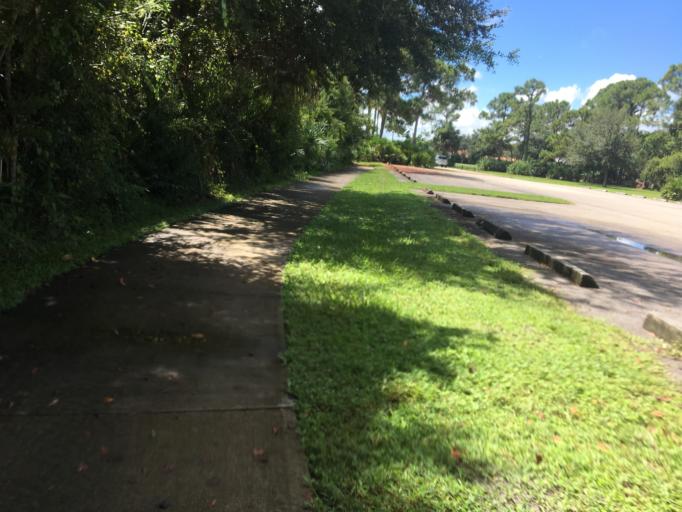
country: US
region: Florida
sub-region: Martin County
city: Palm City
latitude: 27.1799
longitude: -80.2735
